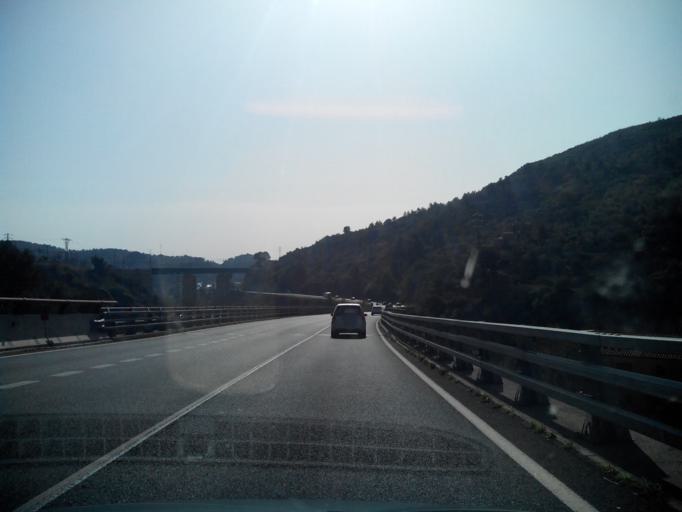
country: ES
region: Catalonia
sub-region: Provincia de Tarragona
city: Alcover
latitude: 41.3078
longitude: 1.1917
